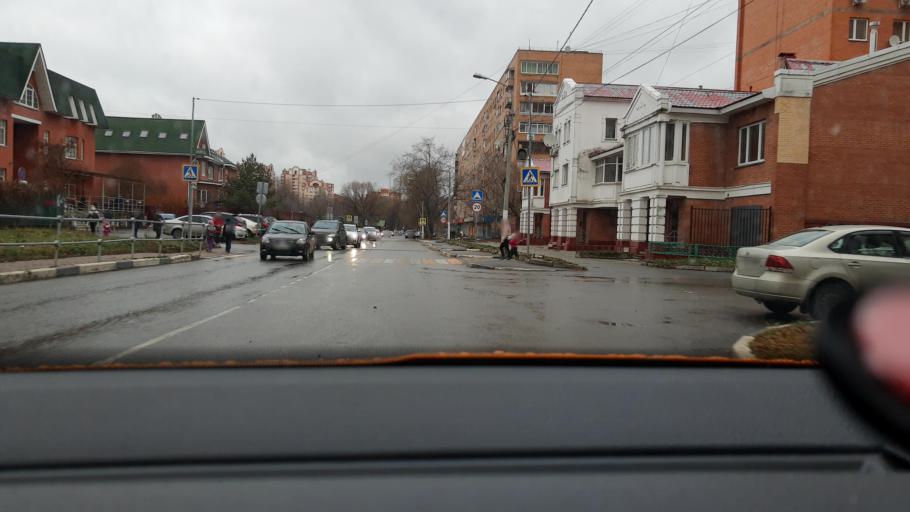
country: RU
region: Moskovskaya
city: Dolgoprudnyy
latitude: 55.9403
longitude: 37.5034
